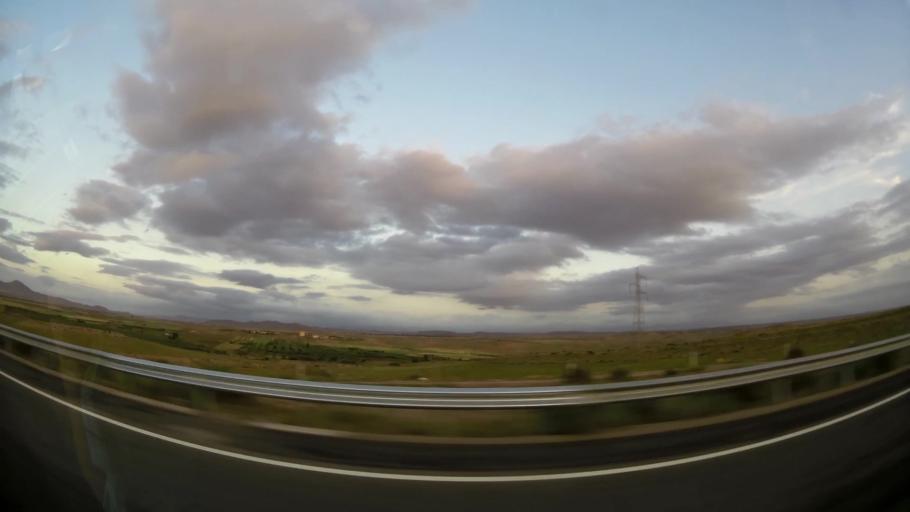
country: MA
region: Oriental
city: Taourirt
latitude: 34.6003
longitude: -2.7735
